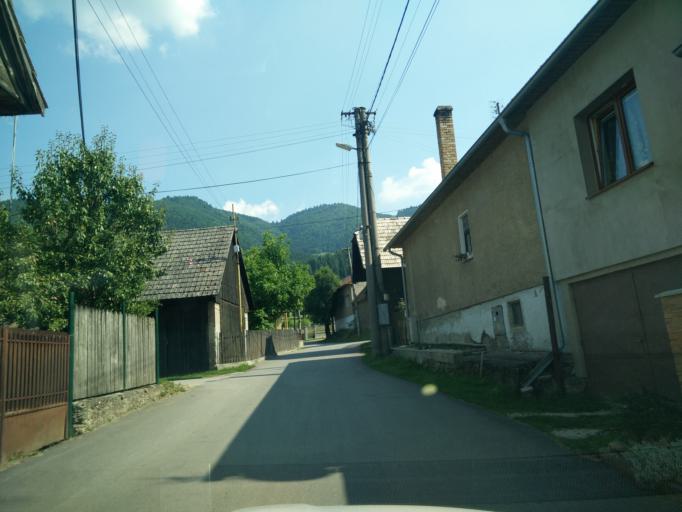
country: SK
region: Zilinsky
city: Rajec
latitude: 49.0591
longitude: 18.6559
